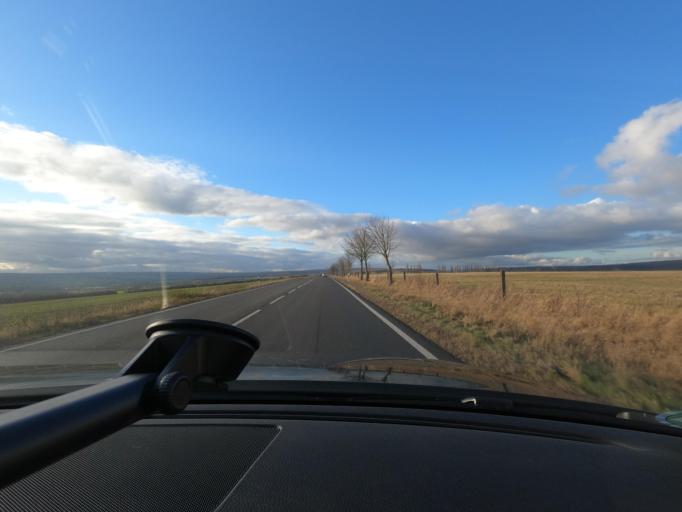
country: DE
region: Thuringia
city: Muehlhausen
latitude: 51.2670
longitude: 10.4254
